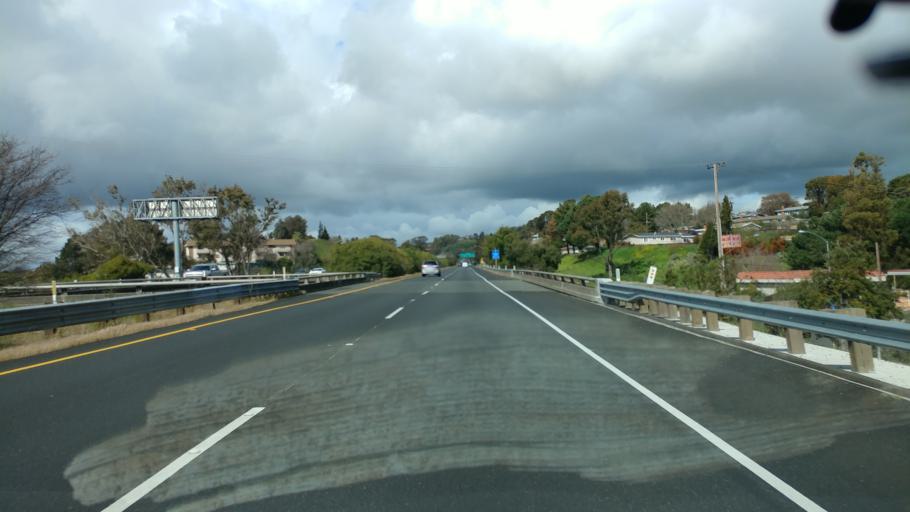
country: US
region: California
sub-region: Solano County
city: Benicia
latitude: 38.0527
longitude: -122.1448
